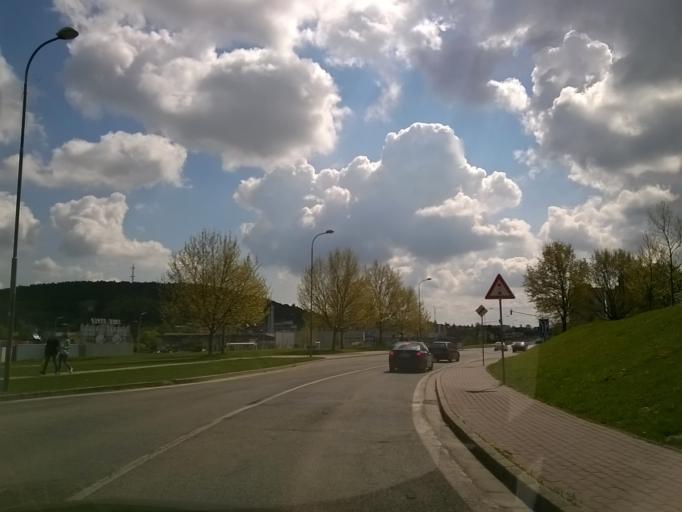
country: SK
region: Nitriansky
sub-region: Okres Nitra
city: Nitra
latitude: 48.3030
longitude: 18.0613
